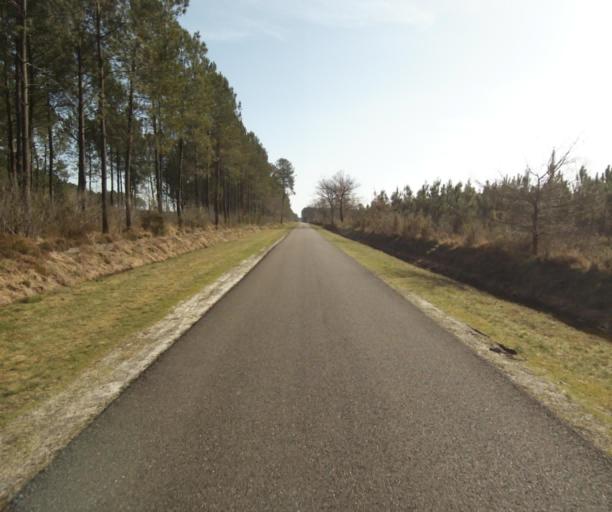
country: FR
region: Aquitaine
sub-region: Departement de la Gironde
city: Grignols
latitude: 44.2292
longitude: -0.1518
